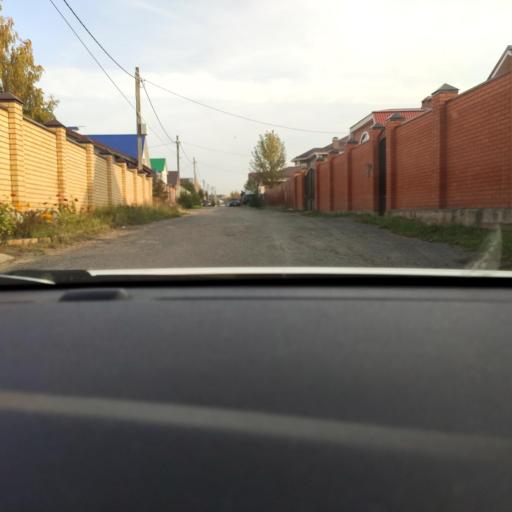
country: RU
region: Tatarstan
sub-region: Gorod Kazan'
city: Kazan
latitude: 55.8232
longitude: 49.2242
